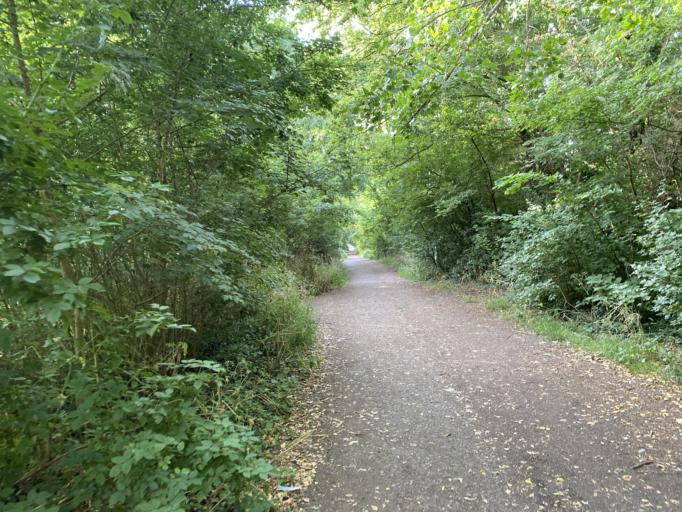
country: GB
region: England
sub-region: Suffolk
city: Haverhill
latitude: 52.0813
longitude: 0.4468
